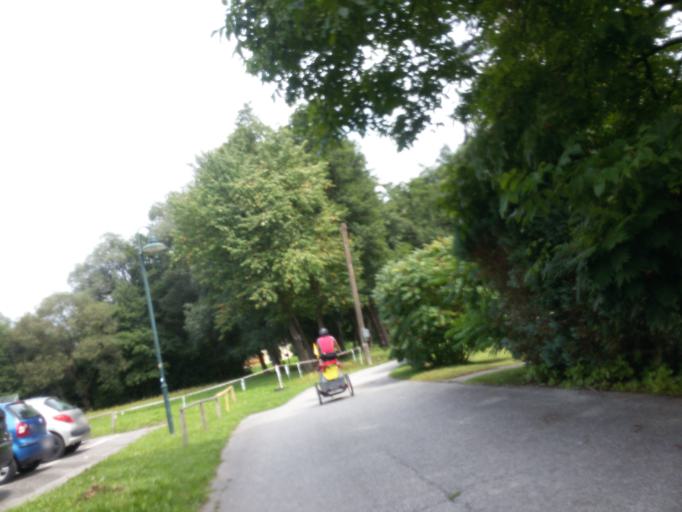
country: AT
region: Carinthia
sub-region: Politischer Bezirk Villach Land
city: Velden am Woerthersee
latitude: 46.6182
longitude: 14.0462
